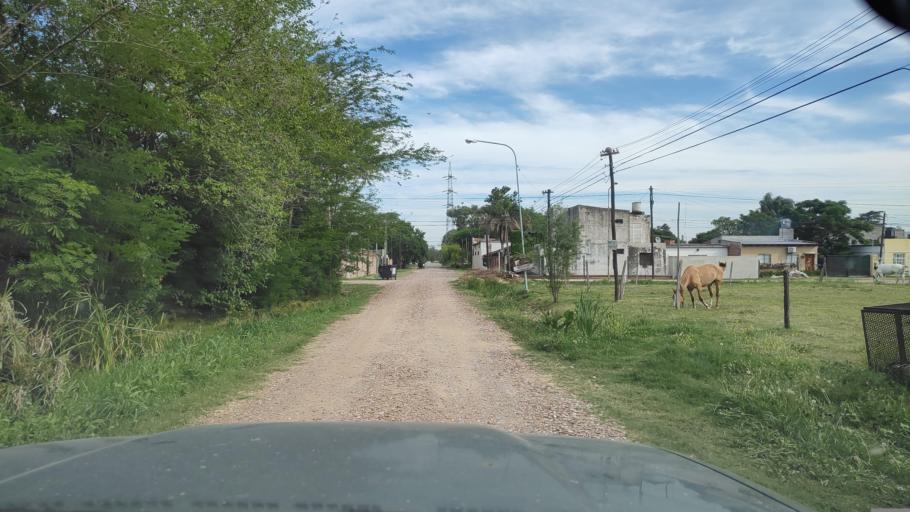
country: AR
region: Buenos Aires
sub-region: Partido de Lujan
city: Lujan
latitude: -34.5790
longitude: -59.0952
